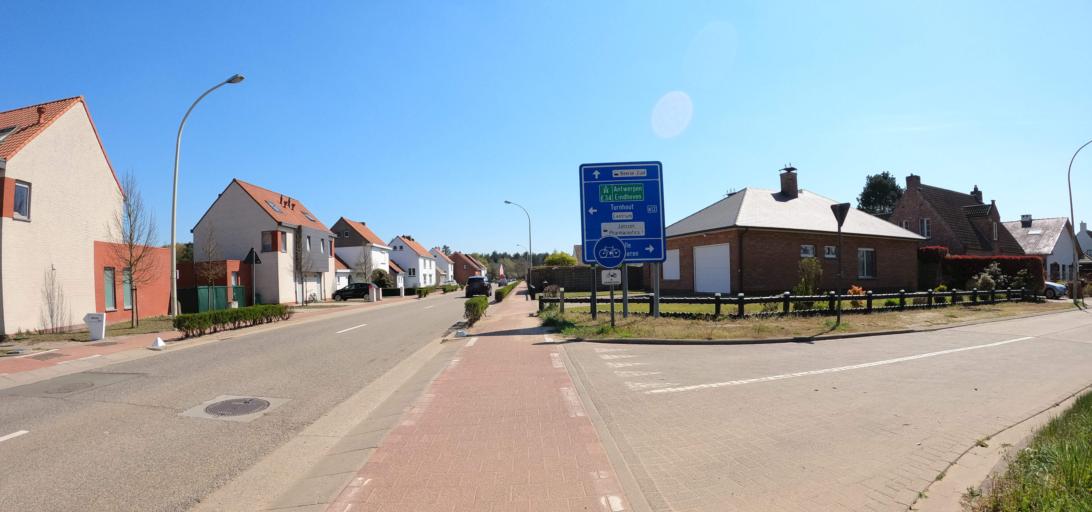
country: BE
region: Flanders
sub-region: Provincie Antwerpen
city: Beerse
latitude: 51.3109
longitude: 4.8395
